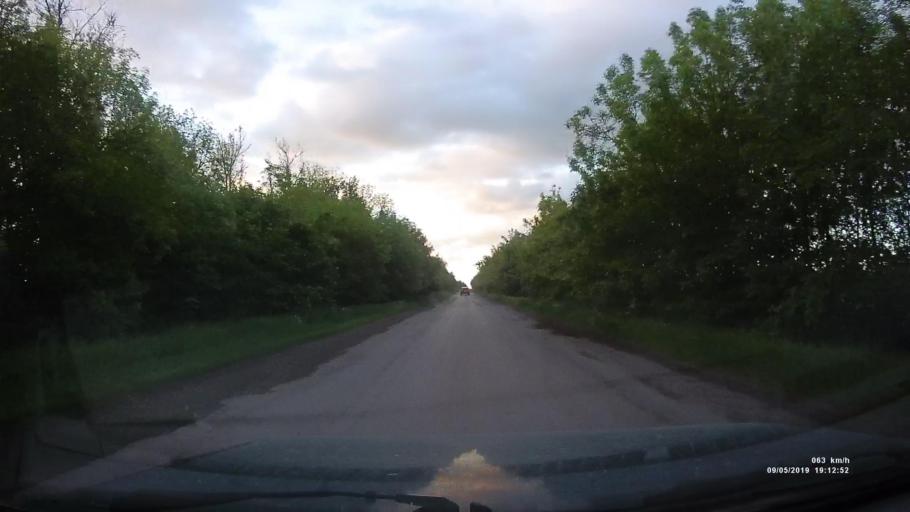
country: RU
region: Krasnodarskiy
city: Kanelovskaya
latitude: 46.7456
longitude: 39.2137
